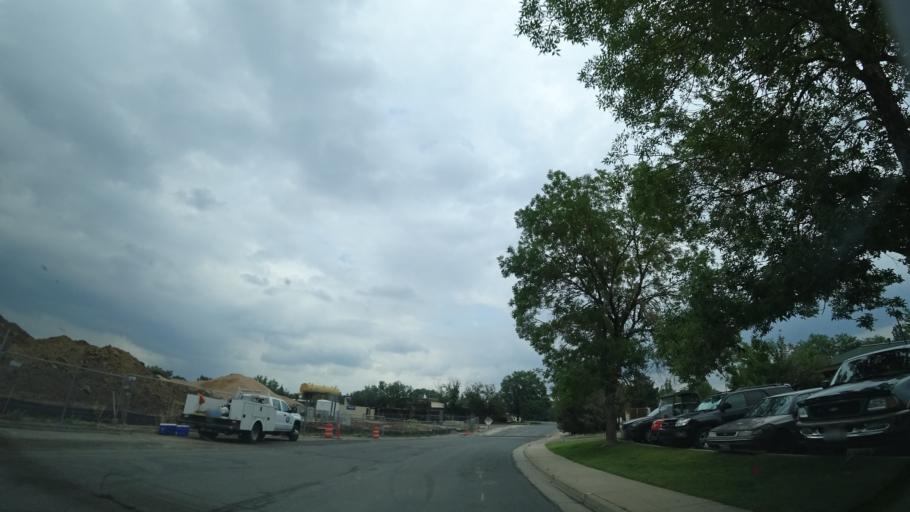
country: US
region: Colorado
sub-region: Jefferson County
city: West Pleasant View
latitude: 39.6997
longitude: -105.1454
